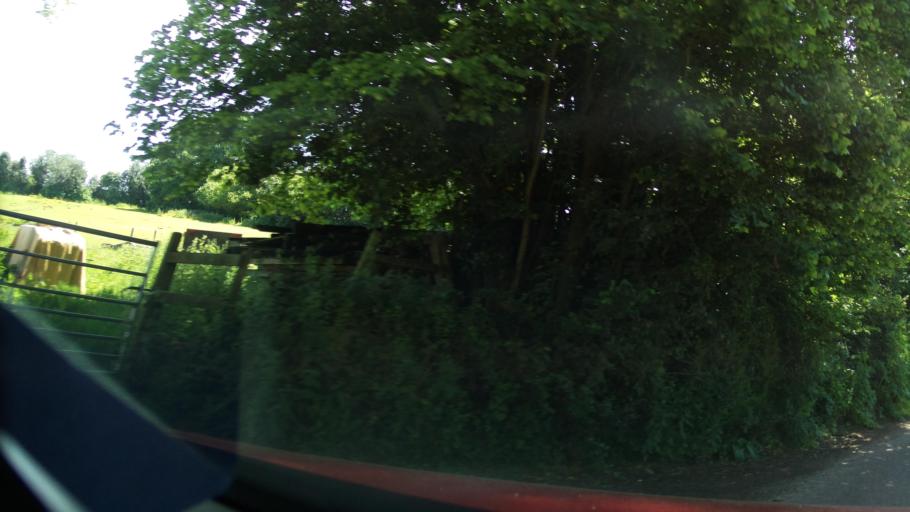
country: GB
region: England
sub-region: Devon
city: Newton Poppleford
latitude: 50.7237
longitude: -3.2835
